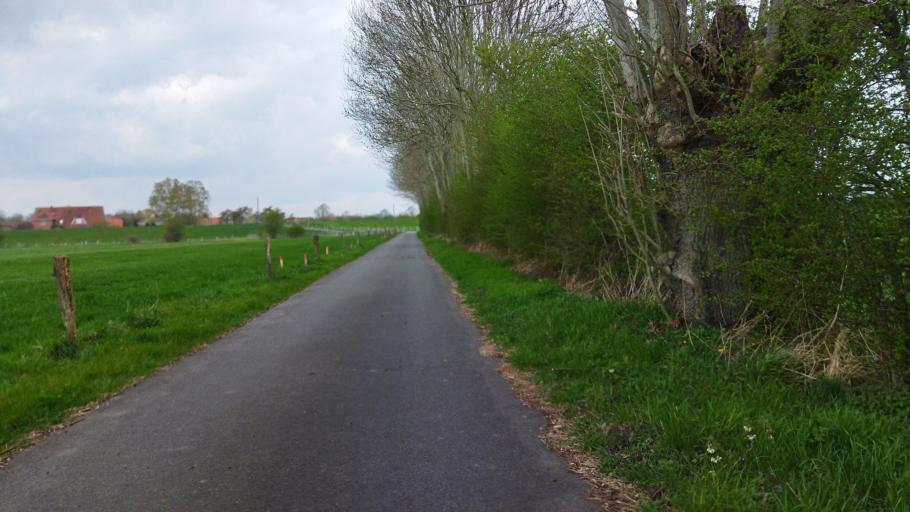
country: DE
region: Lower Saxony
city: Blender
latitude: 52.9091
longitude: 9.1637
